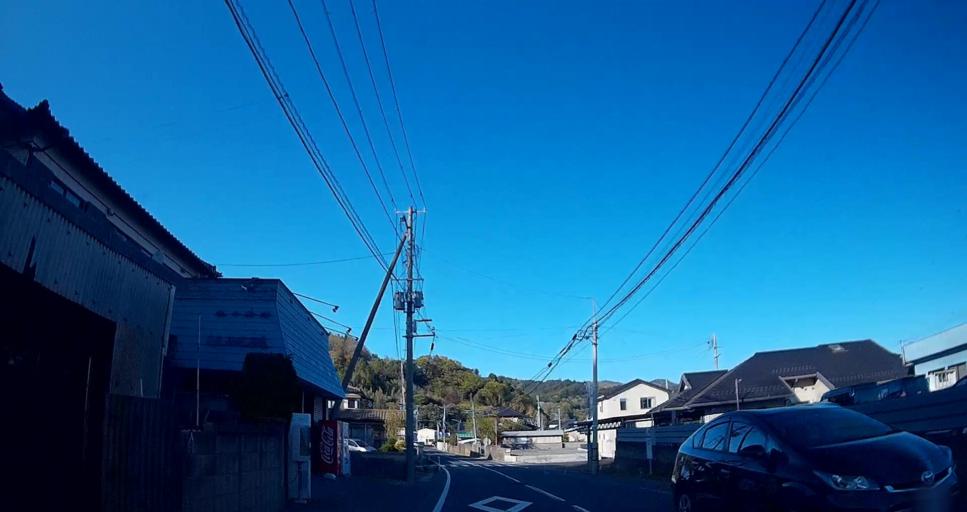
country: JP
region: Miyagi
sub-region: Oshika Gun
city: Onagawa Cho
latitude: 38.4323
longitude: 141.3818
